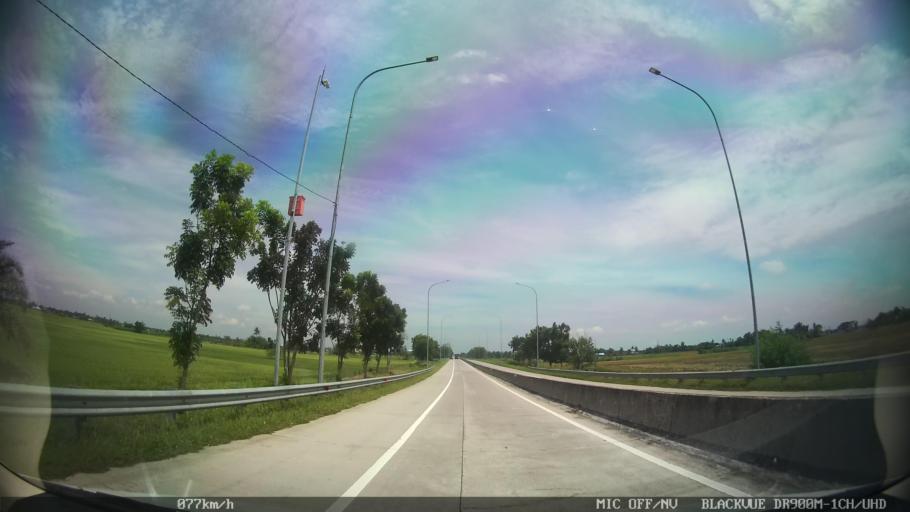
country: ID
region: North Sumatra
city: Perbaungan
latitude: 3.5429
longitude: 98.8911
